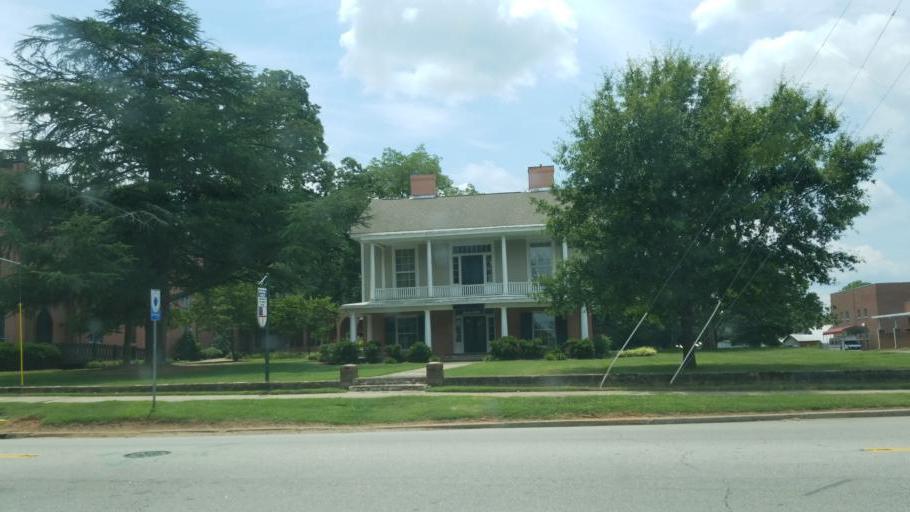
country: US
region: South Carolina
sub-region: York County
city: York
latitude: 34.9932
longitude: -81.2400
